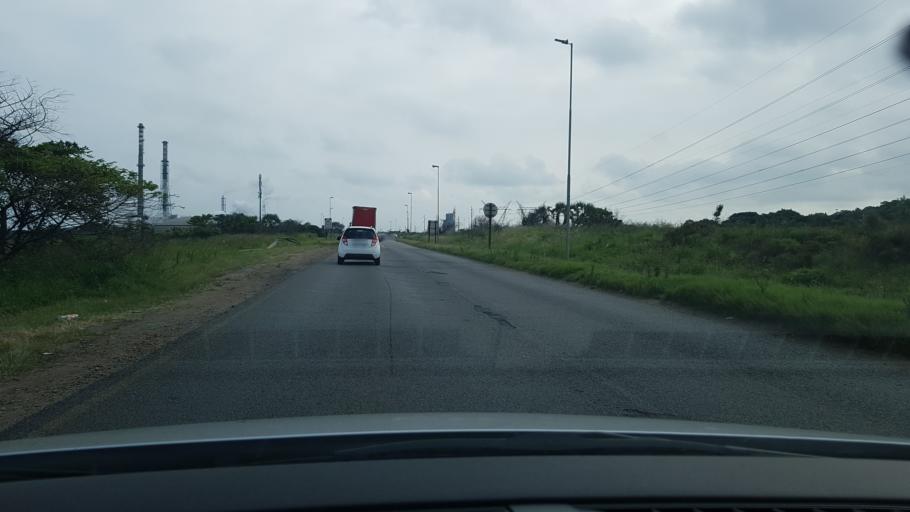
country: ZA
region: KwaZulu-Natal
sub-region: uThungulu District Municipality
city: Richards Bay
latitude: -28.7657
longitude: 32.0371
